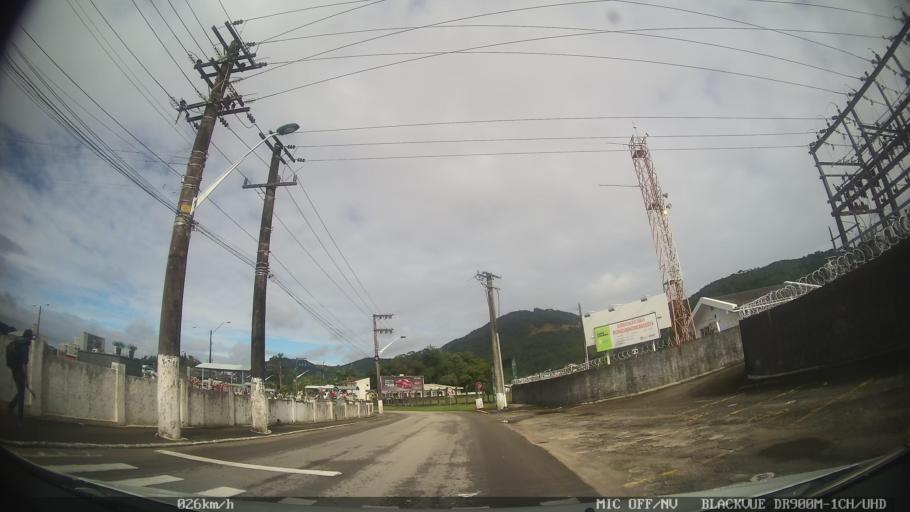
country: BR
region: Santa Catarina
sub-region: Biguacu
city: Biguacu
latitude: -27.5069
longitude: -48.6573
